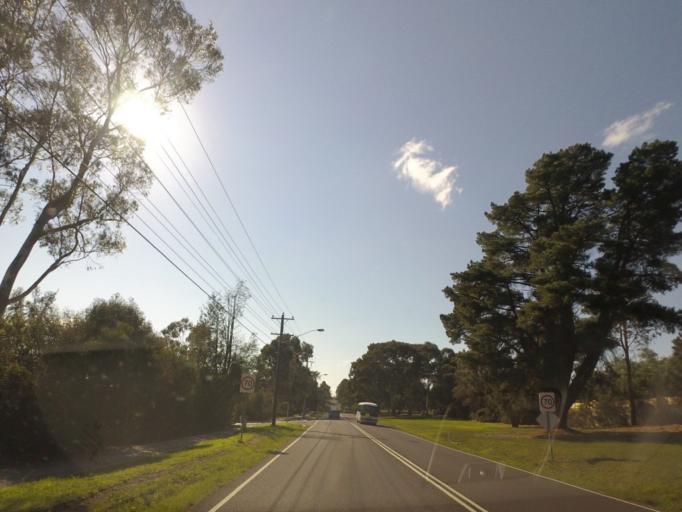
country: AU
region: Victoria
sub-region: Manningham
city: Donvale
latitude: -37.7784
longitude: 145.1824
